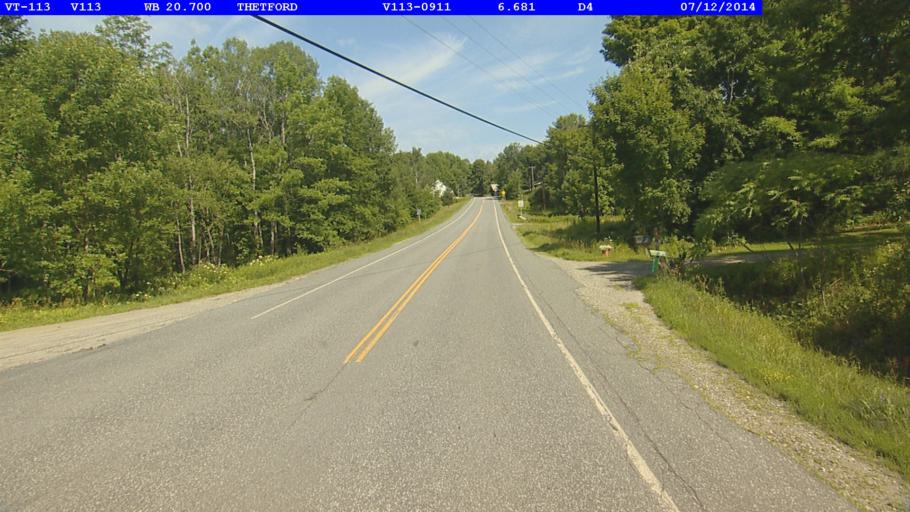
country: US
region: New Hampshire
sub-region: Grafton County
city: Lyme
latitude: 43.8158
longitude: -72.2218
